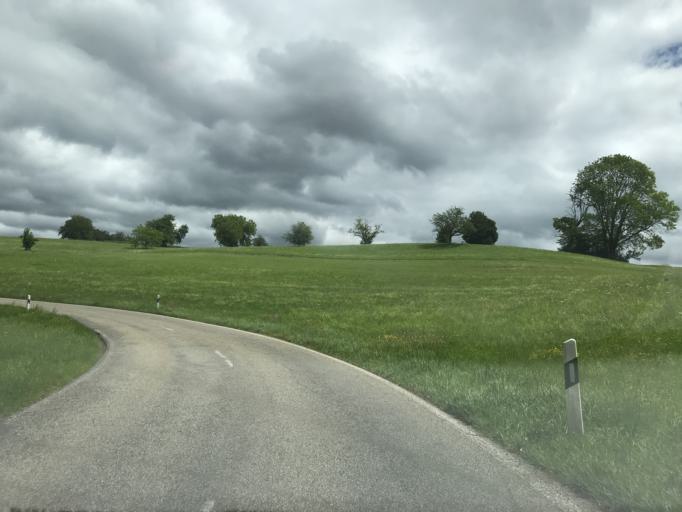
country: DE
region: Baden-Wuerttemberg
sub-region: Freiburg Region
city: Hausen
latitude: 47.6601
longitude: 7.8569
